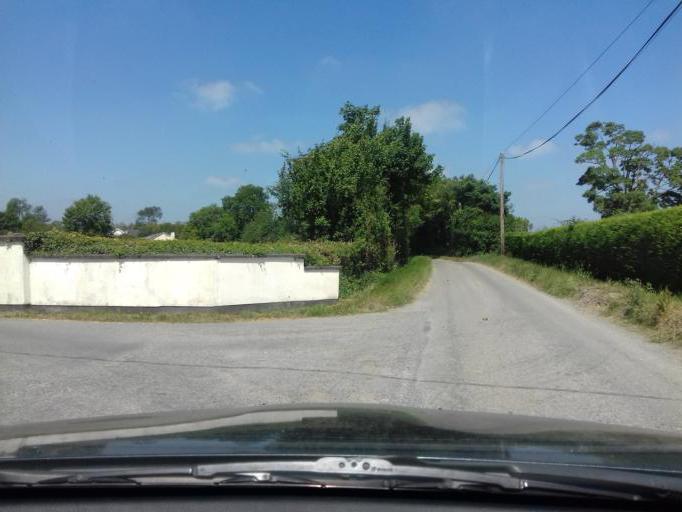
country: IE
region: Leinster
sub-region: Fingal County
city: Swords
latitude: 53.5258
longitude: -6.2355
